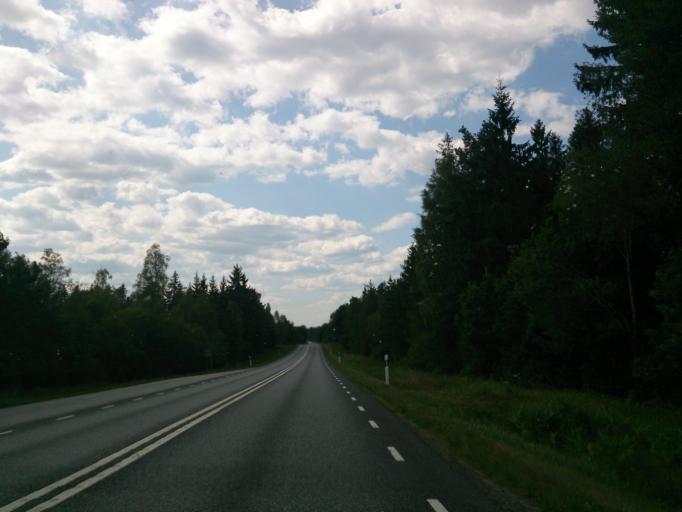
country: SE
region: Joenkoeping
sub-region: Varnamo Kommun
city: Bredaryd
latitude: 57.1742
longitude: 13.6605
